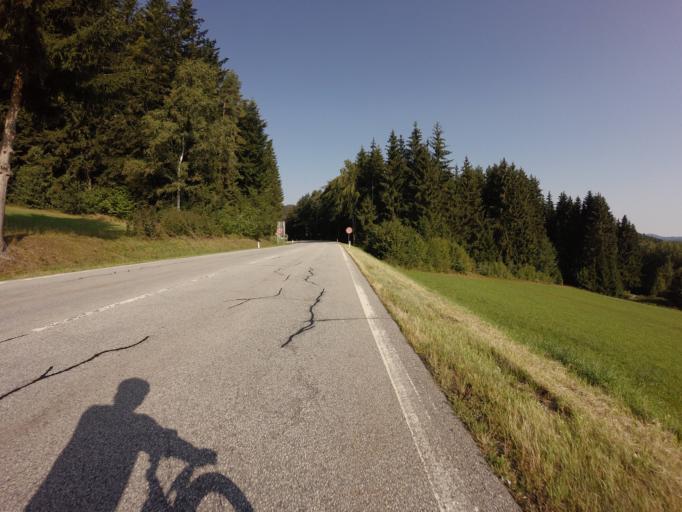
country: AT
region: Upper Austria
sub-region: Politischer Bezirk Urfahr-Umgebung
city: Bad Leonfelden
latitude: 48.5605
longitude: 14.3184
